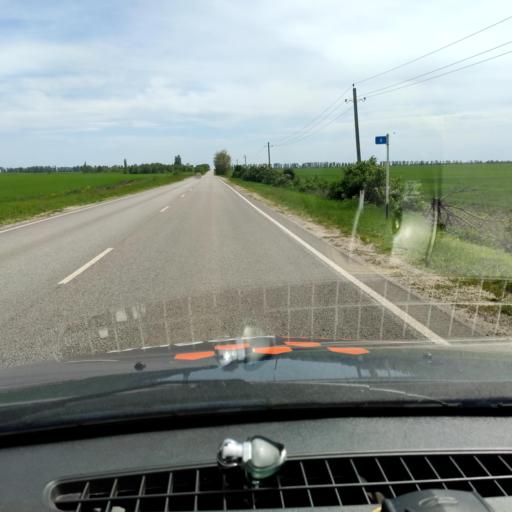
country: RU
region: Voronezj
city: Novaya Usman'
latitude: 51.5791
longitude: 39.3749
